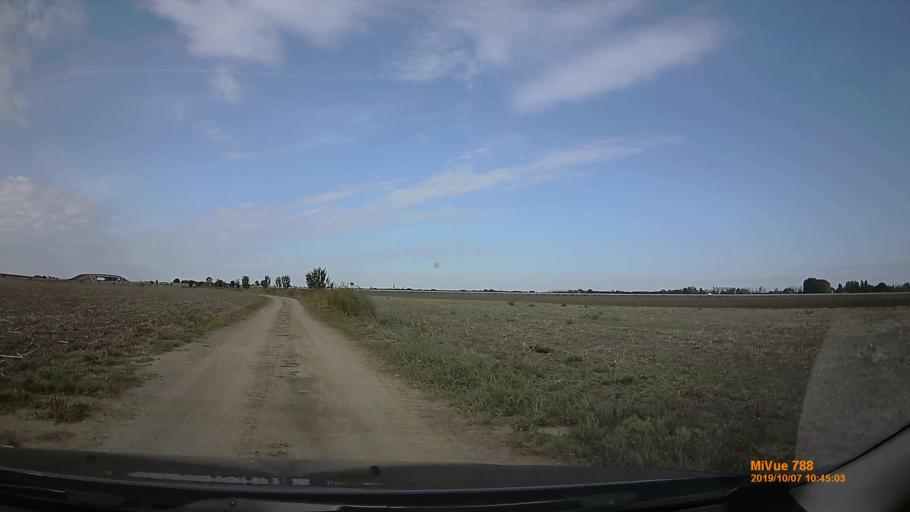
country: HU
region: Bekes
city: Kondoros
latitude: 46.7371
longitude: 20.8244
